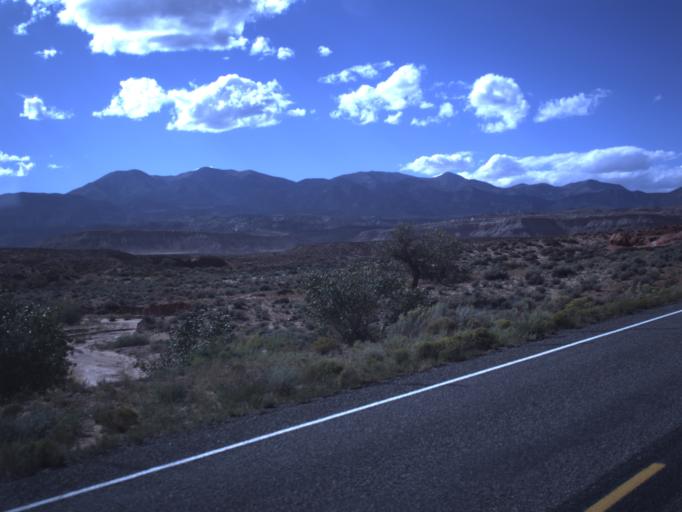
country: US
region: Utah
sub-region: Wayne County
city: Loa
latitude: 38.0616
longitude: -110.5977
